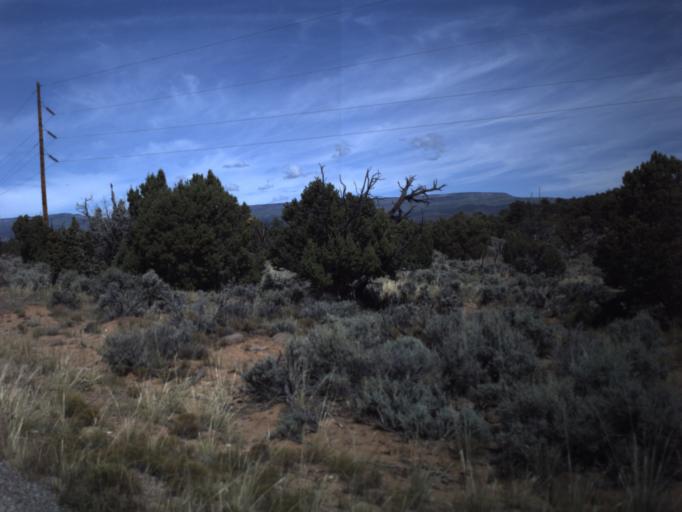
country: US
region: Utah
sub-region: Wayne County
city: Loa
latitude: 37.8630
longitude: -111.4392
